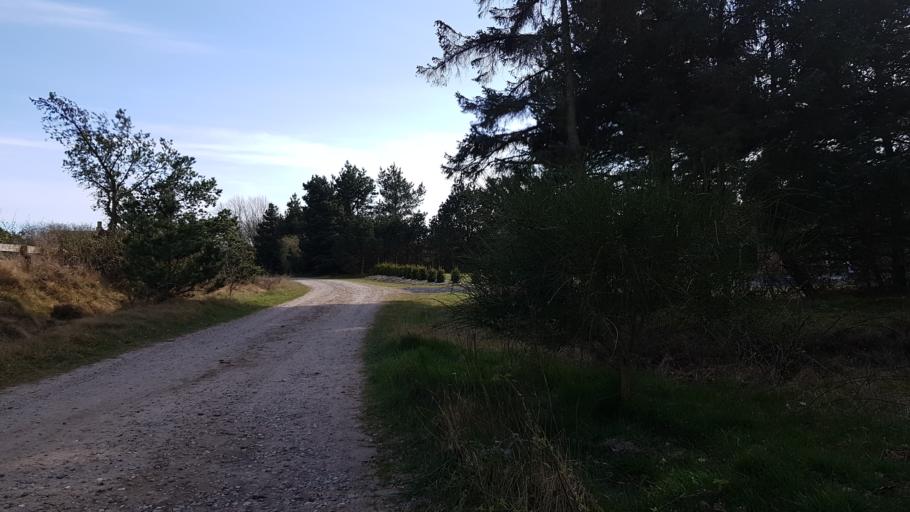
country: DE
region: Schleswig-Holstein
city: List
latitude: 55.1301
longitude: 8.5431
